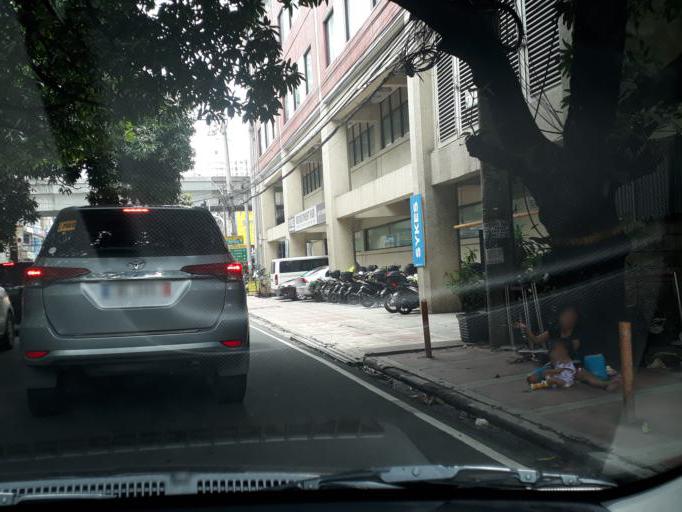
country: PH
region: Metro Manila
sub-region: San Juan
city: San Juan
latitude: 14.6143
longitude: 121.0344
